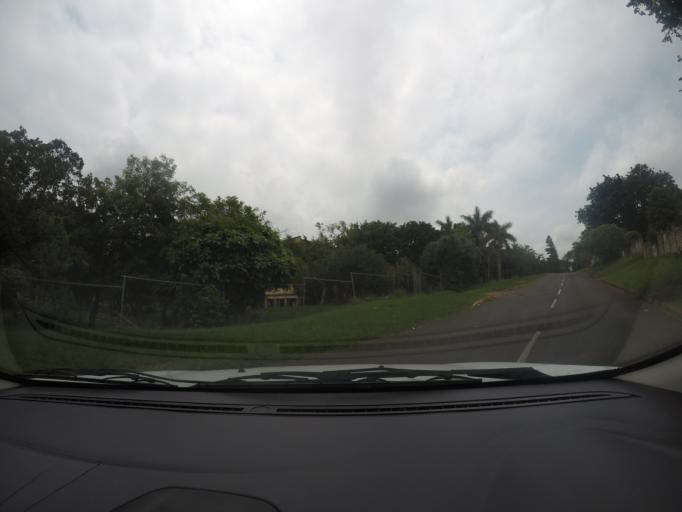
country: ZA
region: KwaZulu-Natal
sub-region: uThungulu District Municipality
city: Empangeni
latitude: -28.7547
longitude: 31.8925
